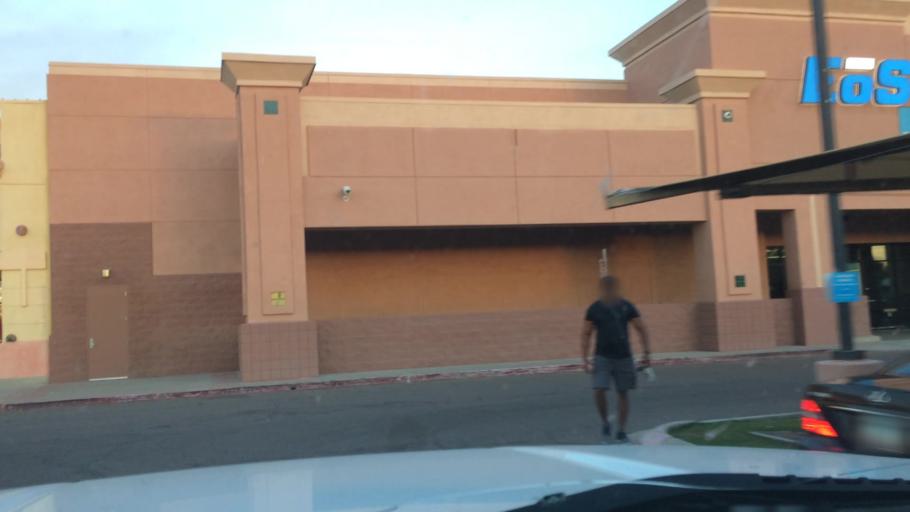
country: US
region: Arizona
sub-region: Maricopa County
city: Peoria
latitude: 33.6703
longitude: -112.1852
